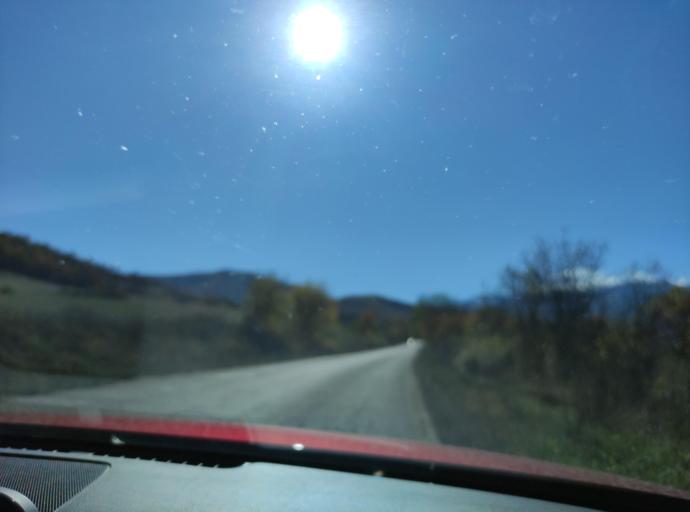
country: BG
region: Montana
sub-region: Obshtina Chiprovtsi
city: Chiprovtsi
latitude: 43.3868
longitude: 22.9220
